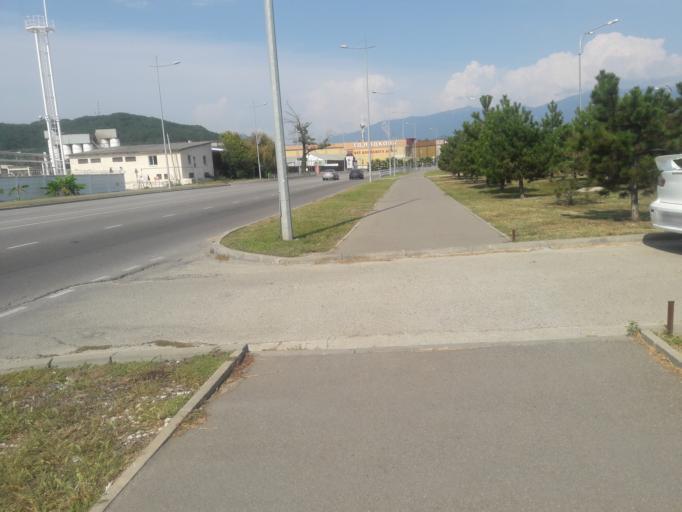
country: RU
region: Krasnodarskiy
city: Vysokoye
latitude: 43.3962
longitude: 39.9915
